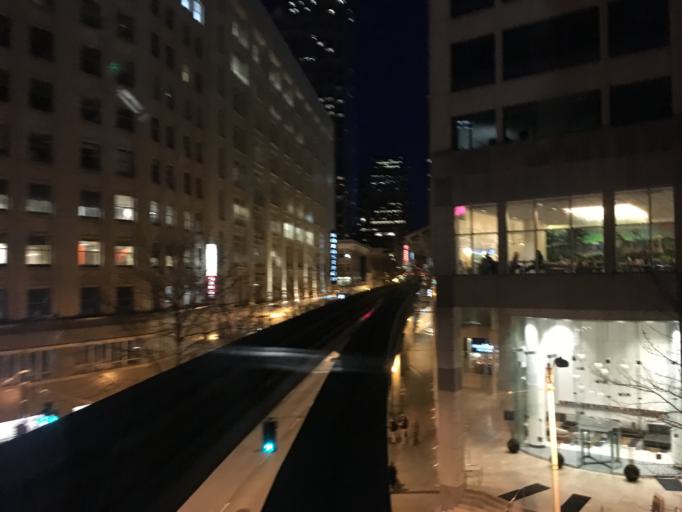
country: US
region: Washington
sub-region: King County
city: Seattle
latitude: 47.6127
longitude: -122.3376
